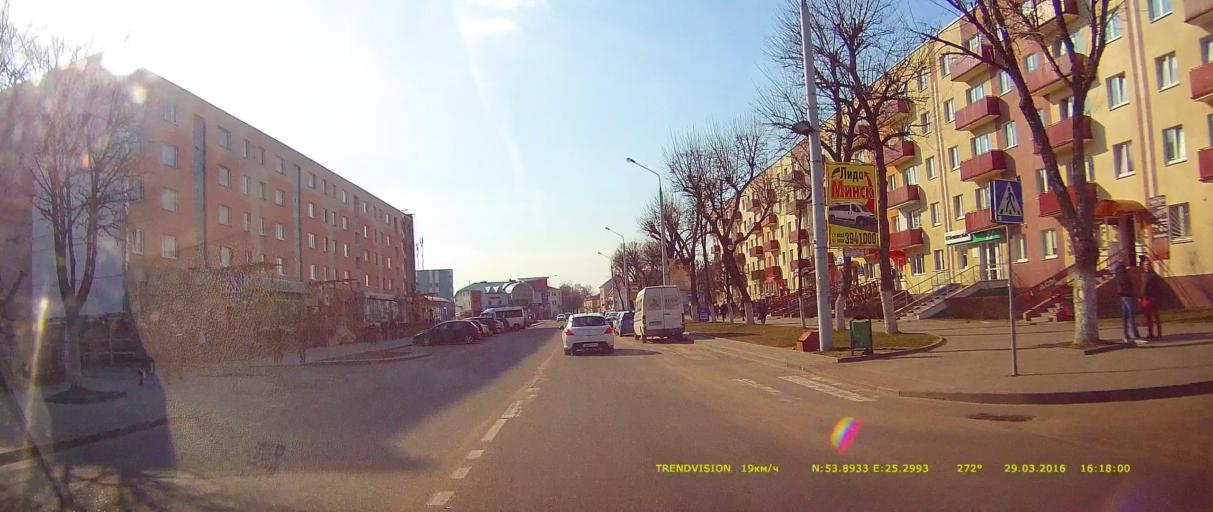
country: BY
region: Grodnenskaya
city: Lida
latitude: 53.8933
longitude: 25.2994
